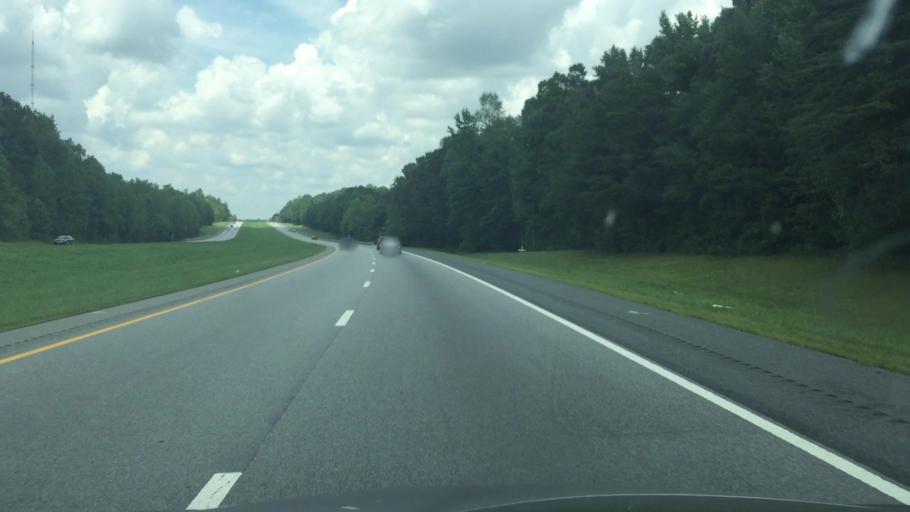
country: US
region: North Carolina
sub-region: Guilford County
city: Pleasant Garden
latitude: 35.9549
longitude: -79.8201
